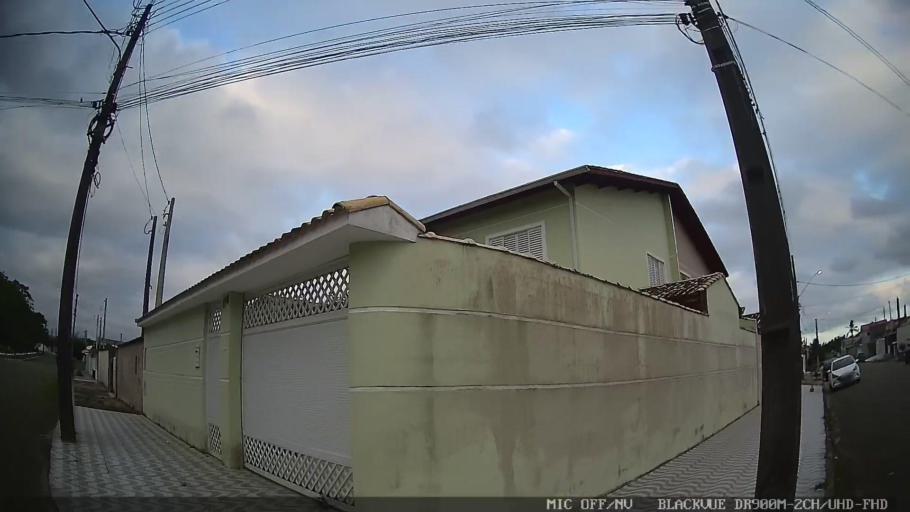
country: BR
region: Sao Paulo
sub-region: Peruibe
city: Peruibe
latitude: -24.3086
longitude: -46.9935
